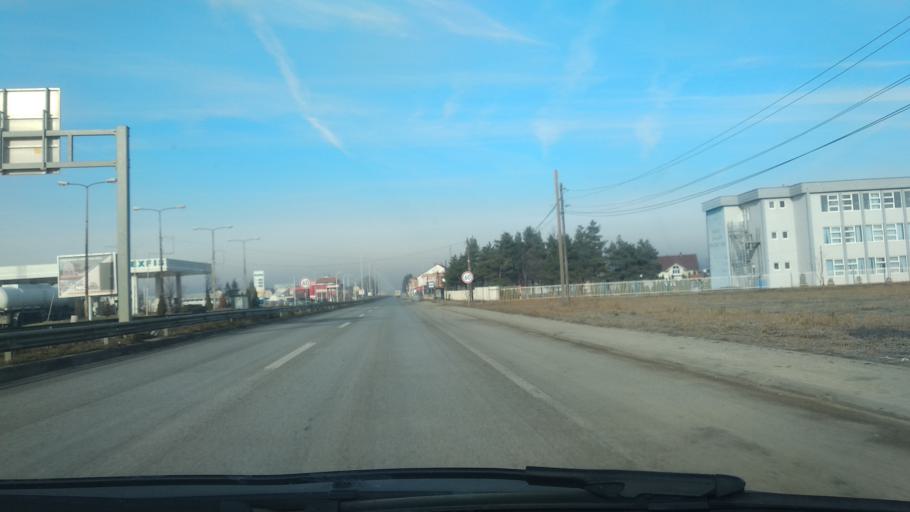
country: XK
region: Pristina
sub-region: Komuna e Obiliqit
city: Obiliq
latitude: 42.7184
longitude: 21.0918
